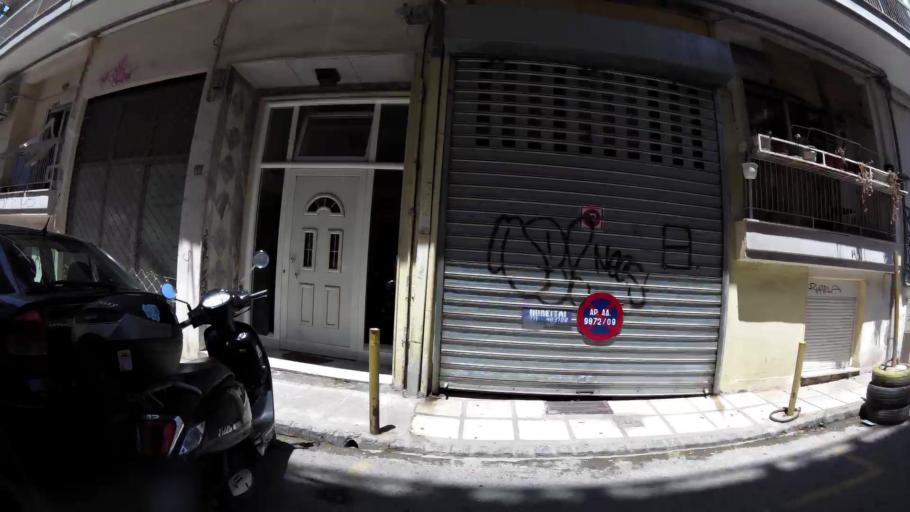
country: GR
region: Central Macedonia
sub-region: Nomos Thessalonikis
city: Triandria
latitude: 40.6135
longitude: 22.9592
